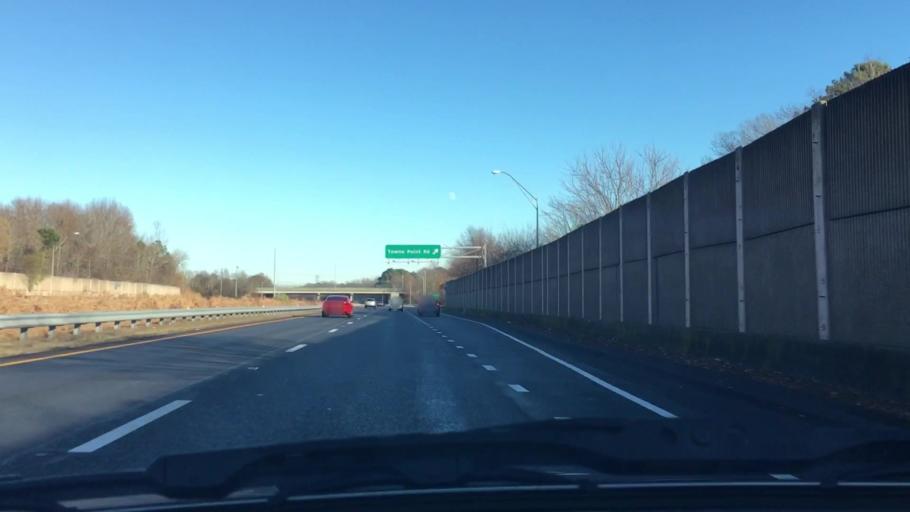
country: US
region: Virginia
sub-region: City of Portsmouth
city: Portsmouth Heights
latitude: 36.8692
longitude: -76.4063
